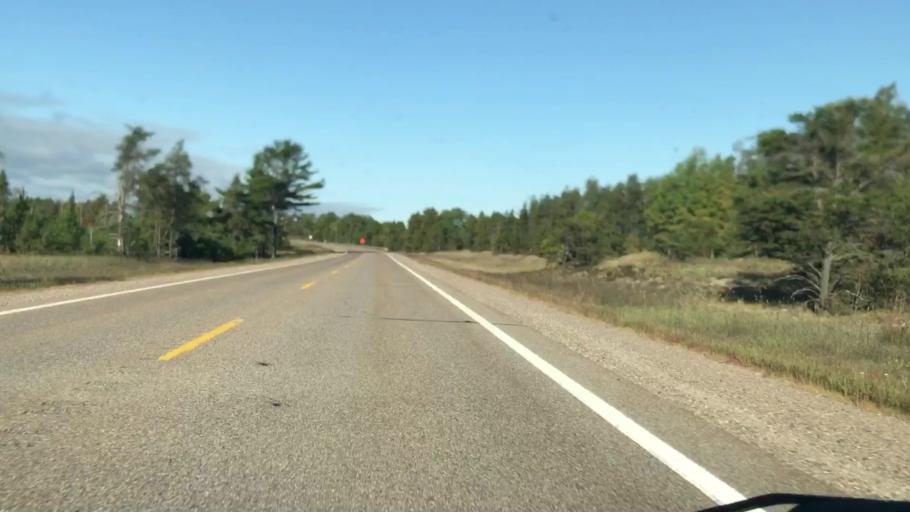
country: US
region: Michigan
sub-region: Mackinac County
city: Saint Ignace
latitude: 46.3583
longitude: -84.8818
